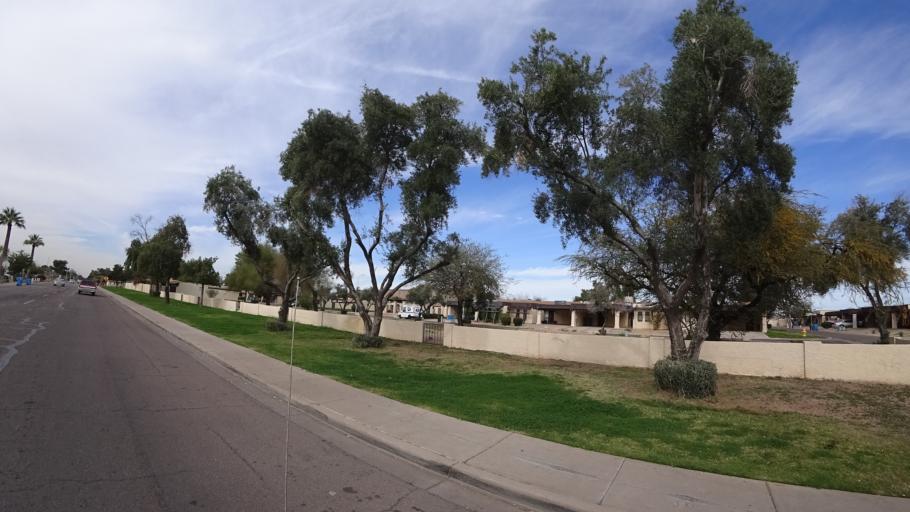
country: US
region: Arizona
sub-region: Maricopa County
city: Glendale
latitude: 33.4877
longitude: -112.1407
